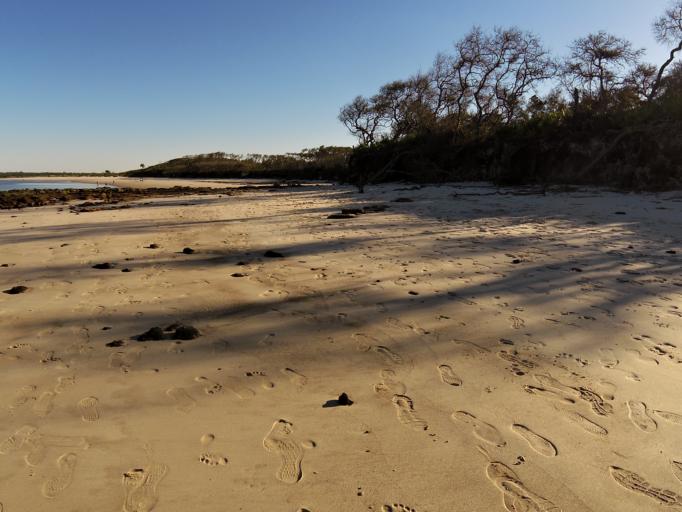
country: US
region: Florida
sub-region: Duval County
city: Atlantic Beach
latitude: 30.4921
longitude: -81.4369
